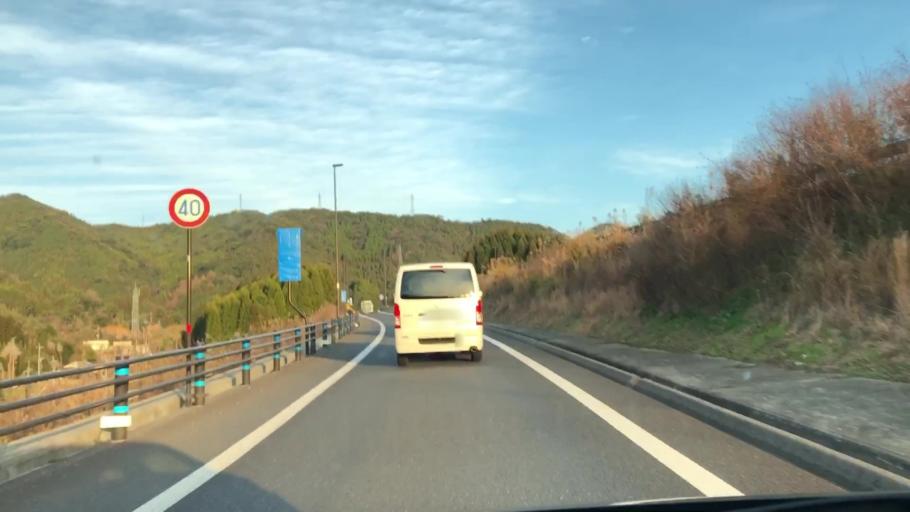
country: JP
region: Kumamoto
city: Minamata
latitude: 32.2428
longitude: 130.4698
